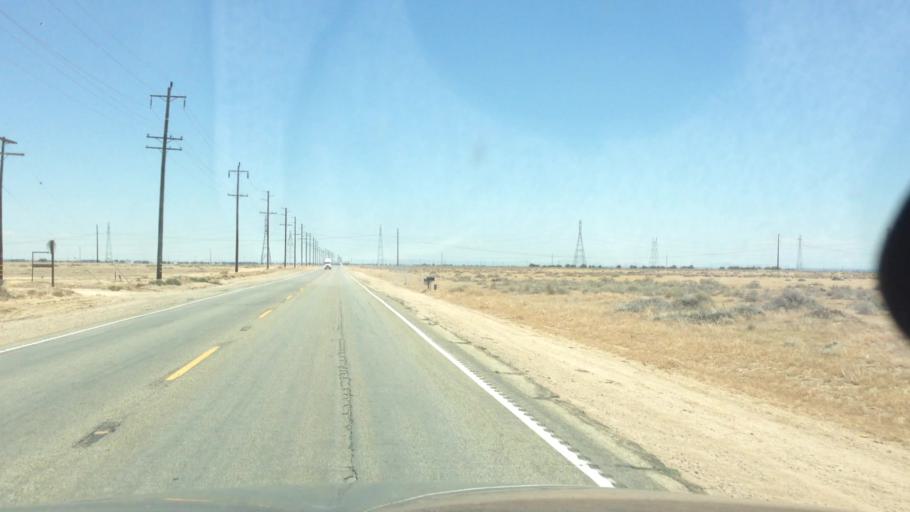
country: US
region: California
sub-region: Los Angeles County
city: Green Valley
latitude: 34.7757
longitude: -118.3529
